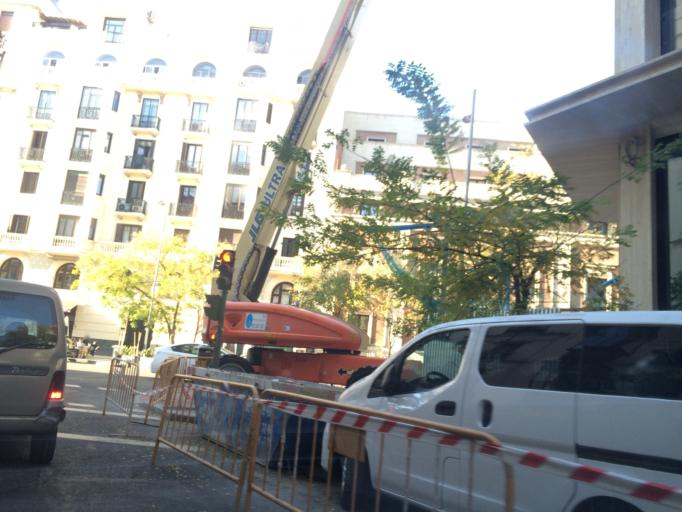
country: ES
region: Madrid
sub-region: Provincia de Madrid
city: Chamberi
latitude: 40.4282
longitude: -3.6946
